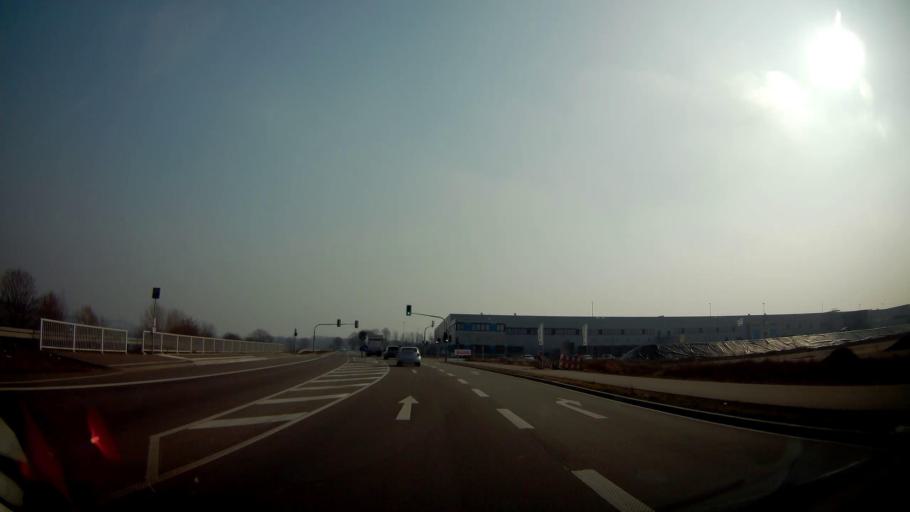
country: DE
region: North Rhine-Westphalia
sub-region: Regierungsbezirk Dusseldorf
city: Moers
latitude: 51.4735
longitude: 6.6817
